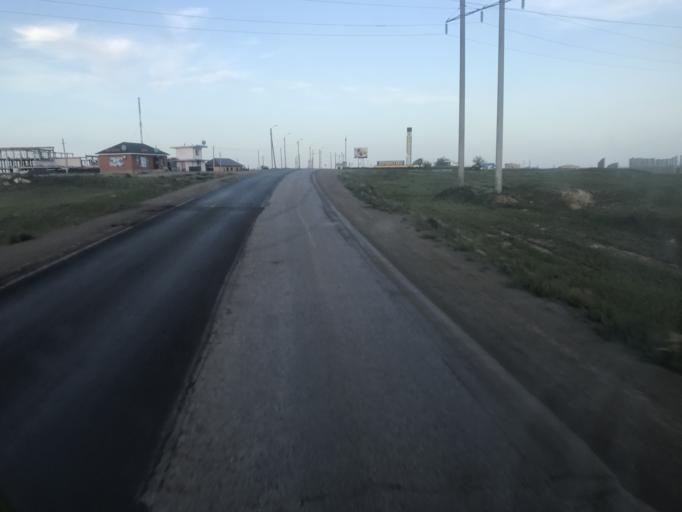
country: KZ
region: Aqtoebe
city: Khromtau
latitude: 50.2588
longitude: 58.4084
